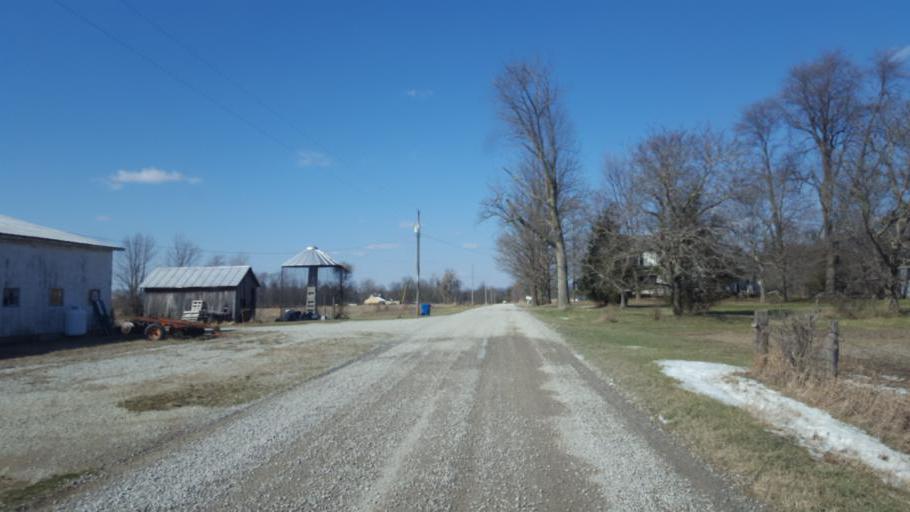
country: US
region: Ohio
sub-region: Morrow County
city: Mount Gilead
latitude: 40.4528
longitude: -82.7262
